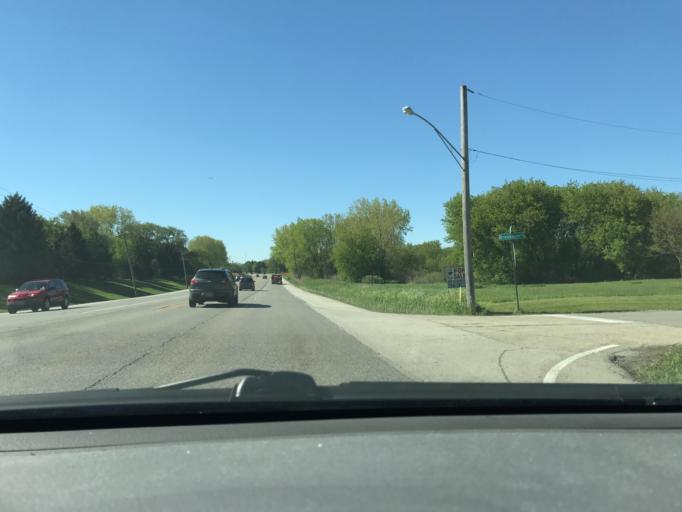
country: US
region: Illinois
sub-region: Kane County
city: Elgin
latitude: 42.0419
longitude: -88.3412
